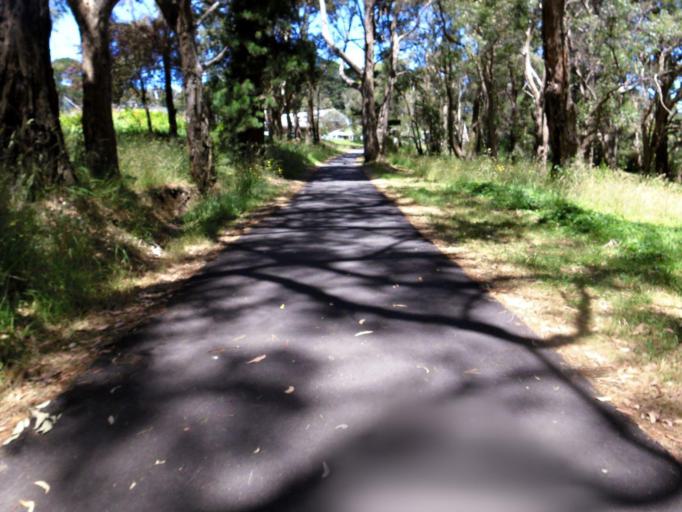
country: AU
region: Victoria
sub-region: Mornington Peninsula
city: Merricks
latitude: -38.3792
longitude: 145.0260
